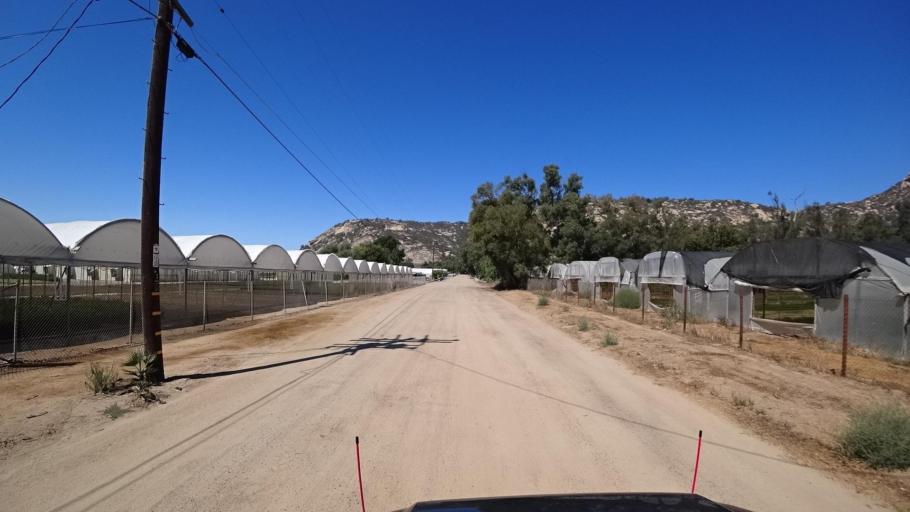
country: US
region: California
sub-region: San Diego County
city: Rainbow
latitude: 33.4213
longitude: -117.1488
